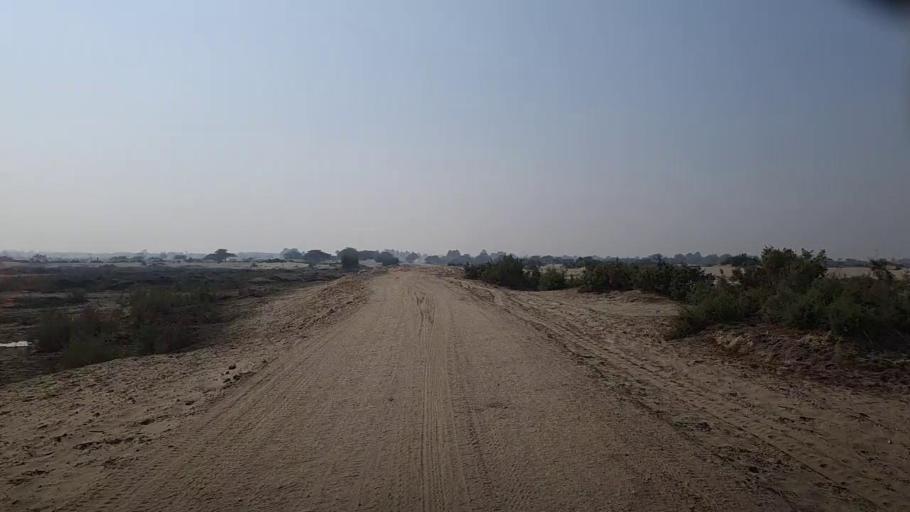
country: PK
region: Sindh
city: Bozdar
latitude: 27.2196
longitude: 68.5827
